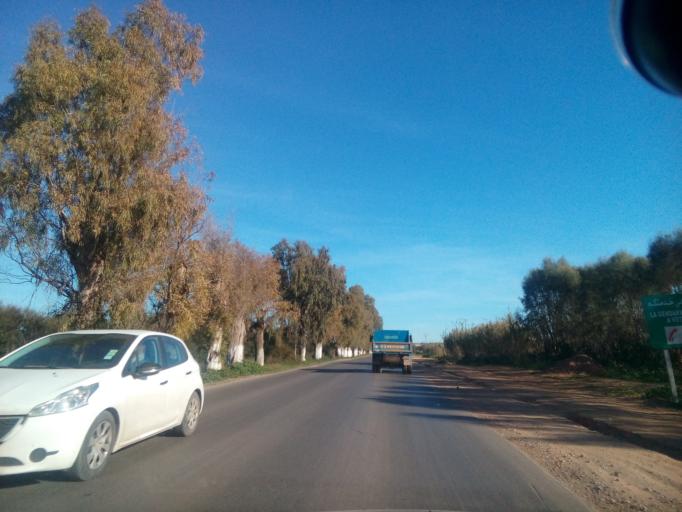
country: DZ
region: Mostaganem
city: Mostaganem
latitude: 35.9010
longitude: 0.2185
